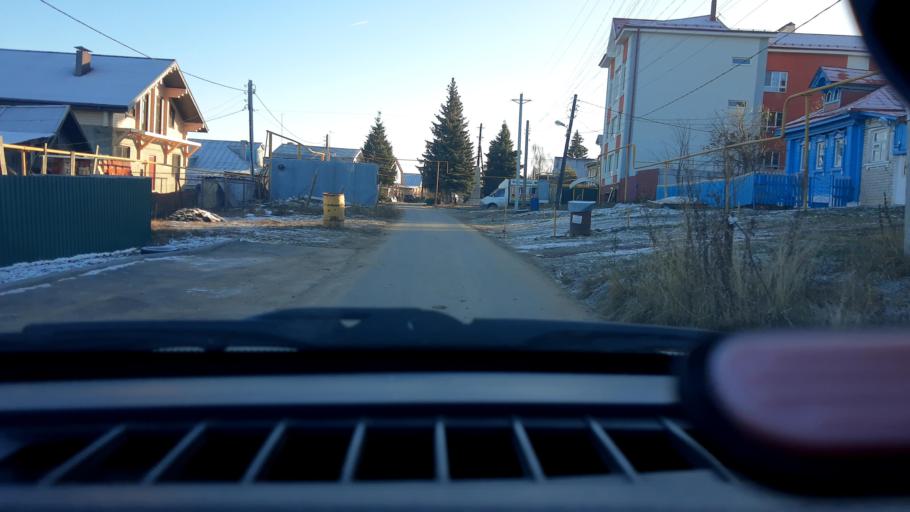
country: RU
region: Nizjnij Novgorod
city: Afonino
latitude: 56.3078
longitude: 44.0876
